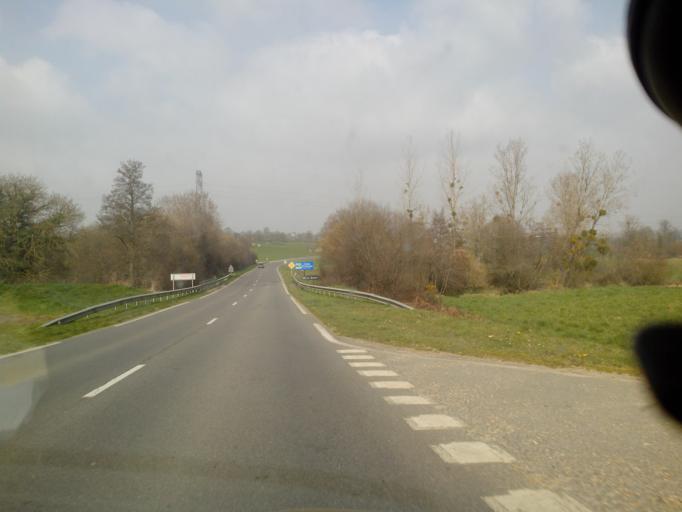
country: FR
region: Brittany
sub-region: Departement d'Ille-et-Vilaine
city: Quedillac
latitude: 48.2535
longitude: -2.1672
